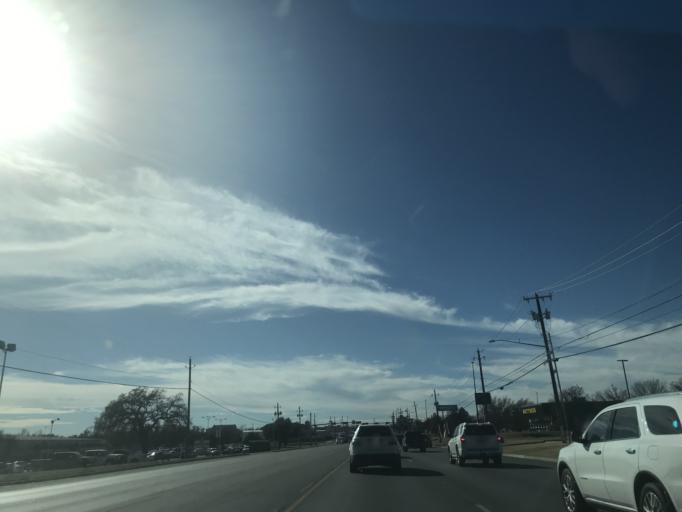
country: US
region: Texas
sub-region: Erath County
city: Stephenville
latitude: 32.2056
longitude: -98.2344
